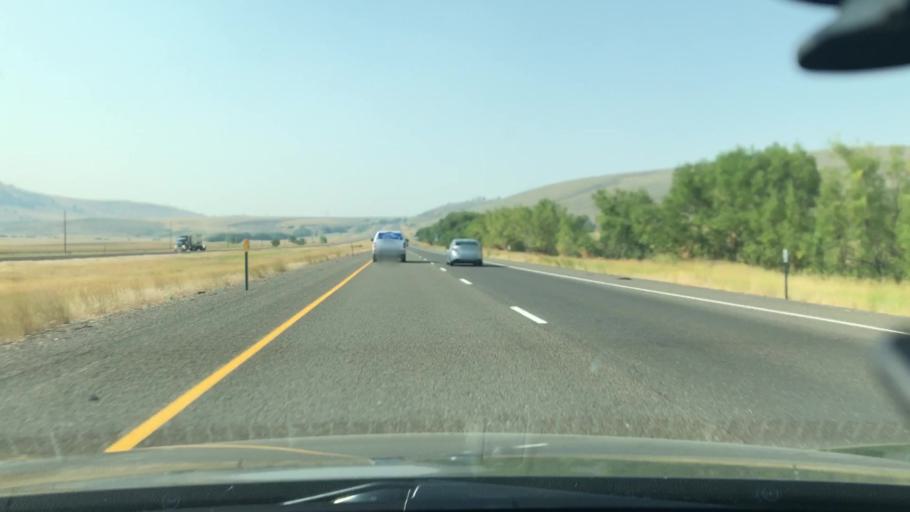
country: US
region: Oregon
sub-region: Union County
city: Union
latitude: 45.1292
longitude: -117.9644
